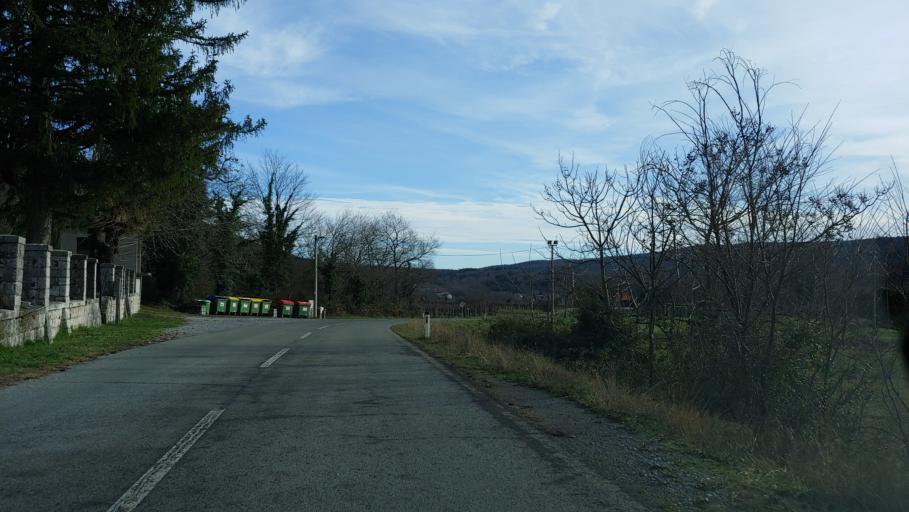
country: IT
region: Friuli Venezia Giulia
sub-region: Provincia di Trieste
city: Sistiana-Visogliano
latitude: 45.8146
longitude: 13.6303
